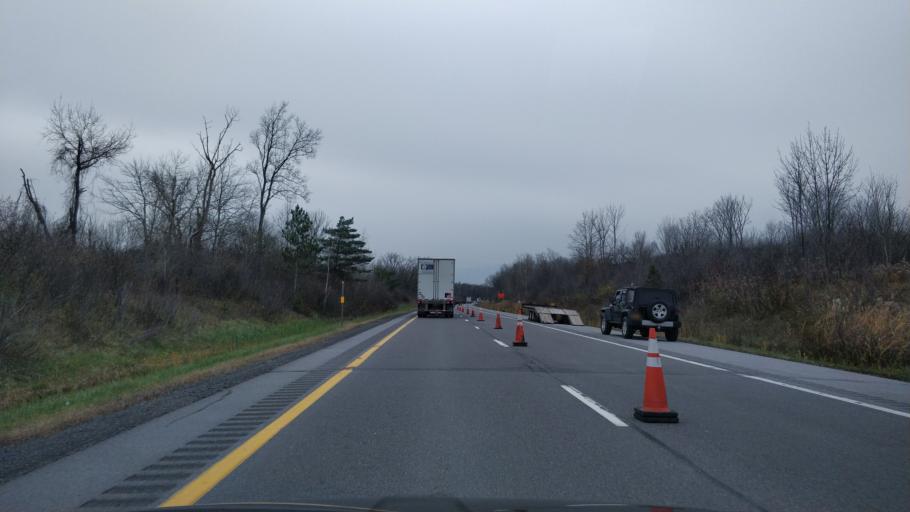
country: US
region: New York
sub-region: Oswego County
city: Pulaski
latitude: 43.6270
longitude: -76.0830
